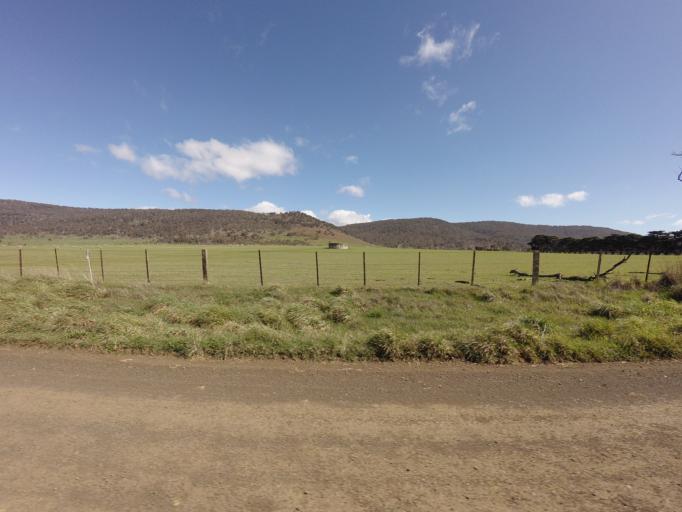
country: AU
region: Tasmania
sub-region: Northern Midlands
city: Evandale
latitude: -41.9519
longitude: 147.4352
